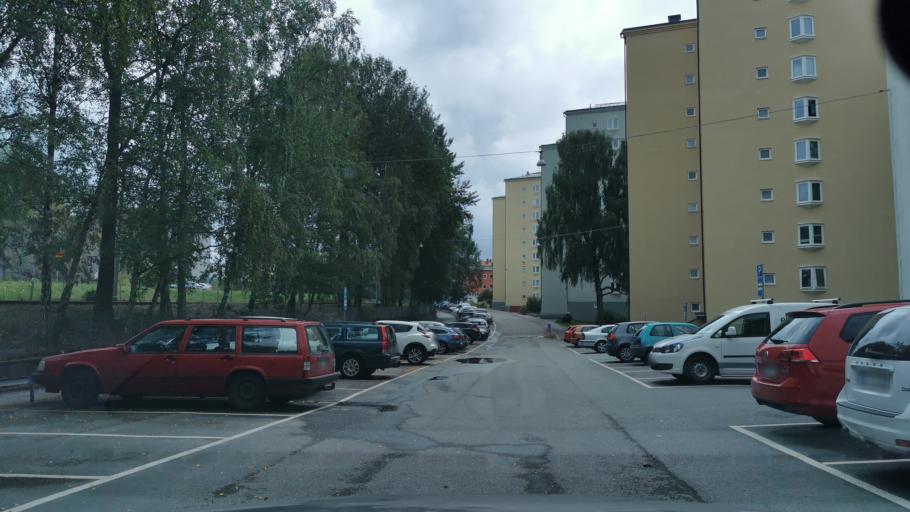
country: SE
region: Vaestra Goetaland
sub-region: Goteborg
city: Goeteborg
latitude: 57.6860
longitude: 11.9709
